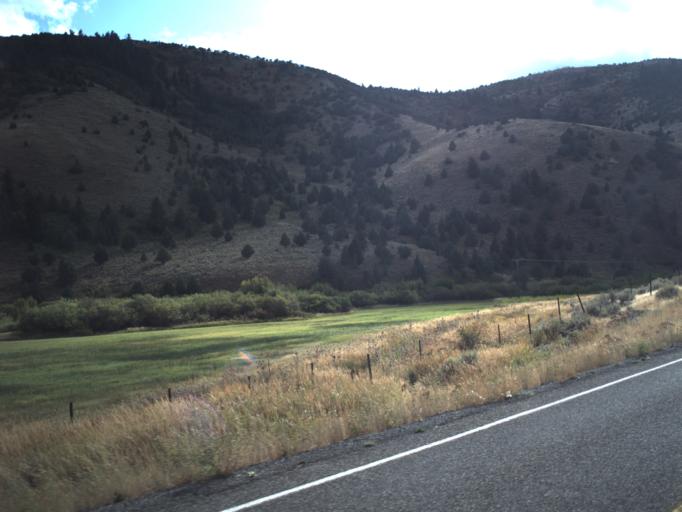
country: US
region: Utah
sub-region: Cache County
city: Millville
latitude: 41.6058
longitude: -111.5857
